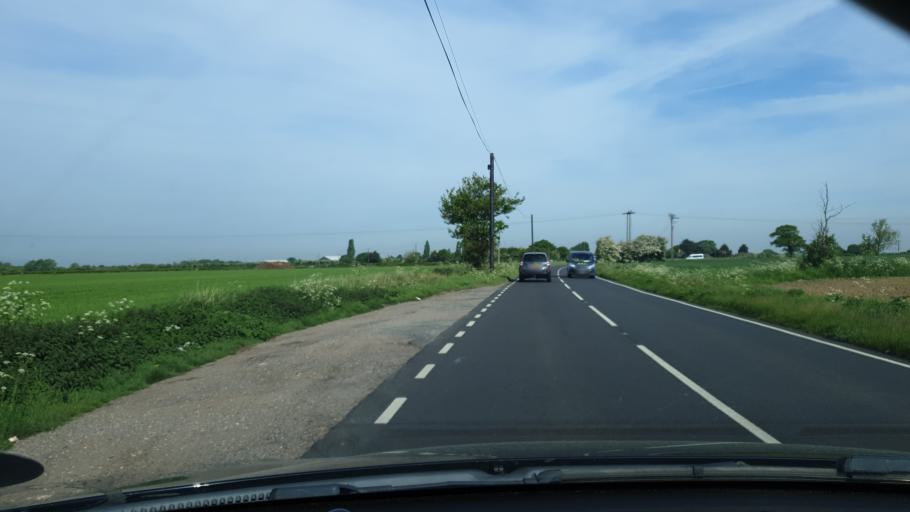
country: GB
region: England
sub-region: Essex
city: Frinton-on-Sea
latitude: 51.8478
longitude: 1.1925
